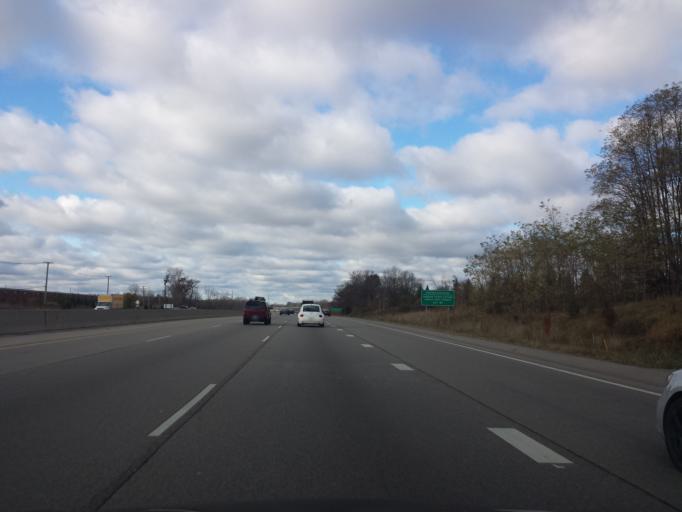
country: US
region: Michigan
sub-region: Oakland County
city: Auburn Hills
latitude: 42.6450
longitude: -83.2036
